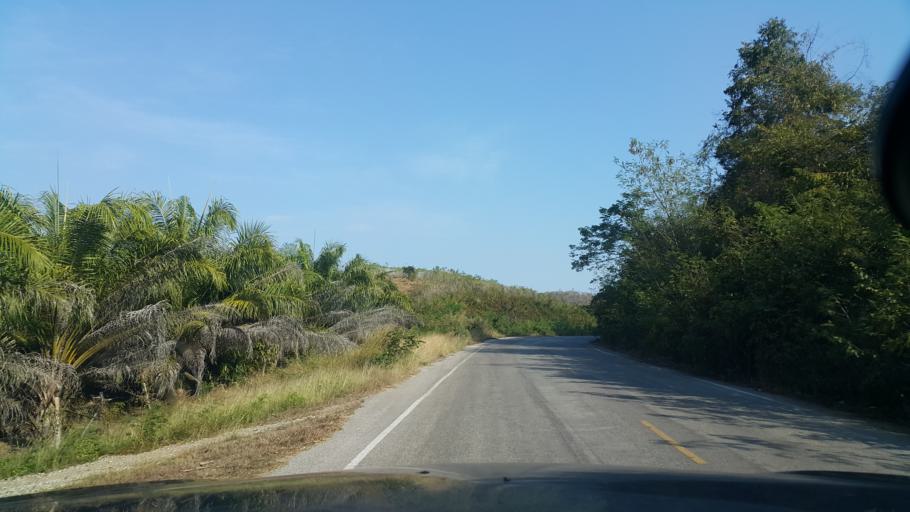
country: TH
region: Loei
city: Chiang Khan
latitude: 17.8338
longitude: 101.6266
